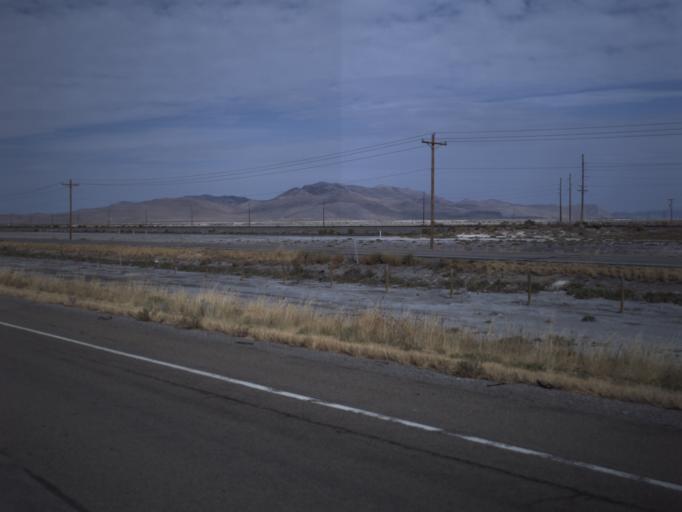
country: US
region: Utah
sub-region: Tooele County
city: Grantsville
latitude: 40.7468
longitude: -112.6597
